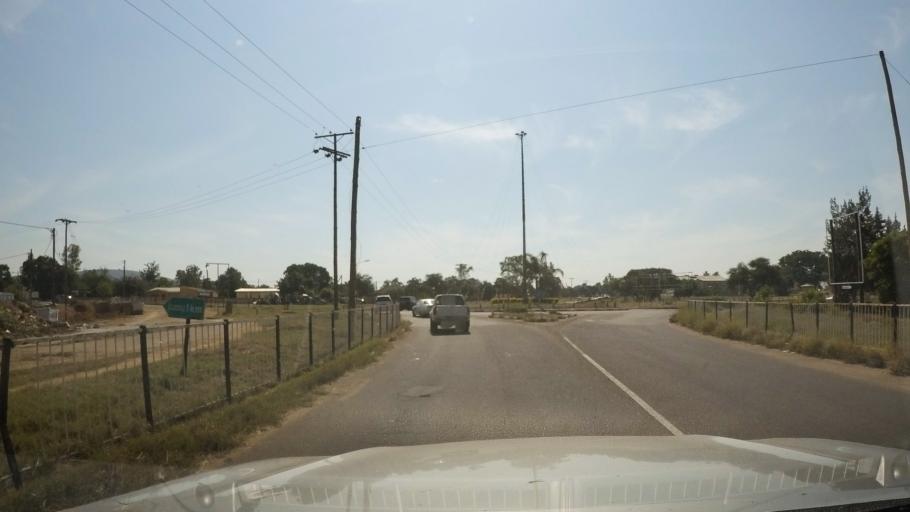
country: BW
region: South East
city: Lobatse
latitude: -25.2144
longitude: 25.6821
